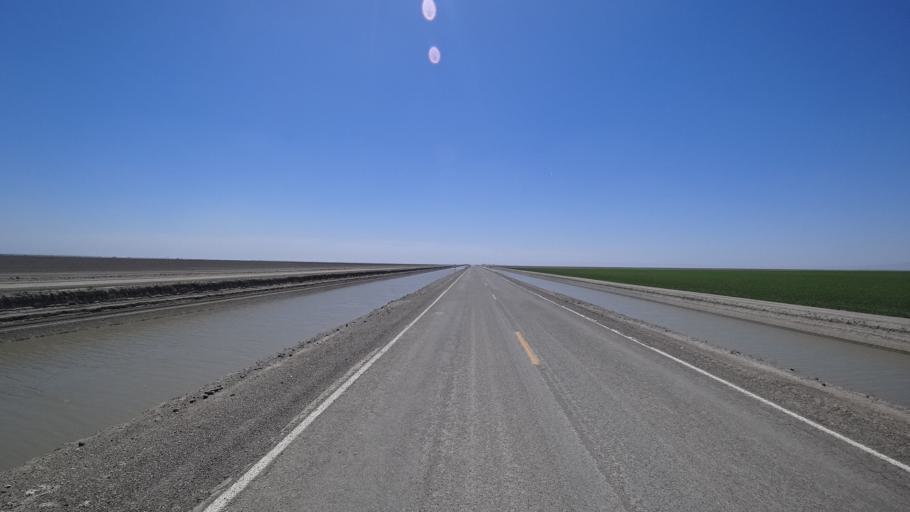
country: US
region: California
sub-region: Kings County
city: Corcoran
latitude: 35.9891
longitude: -119.6431
